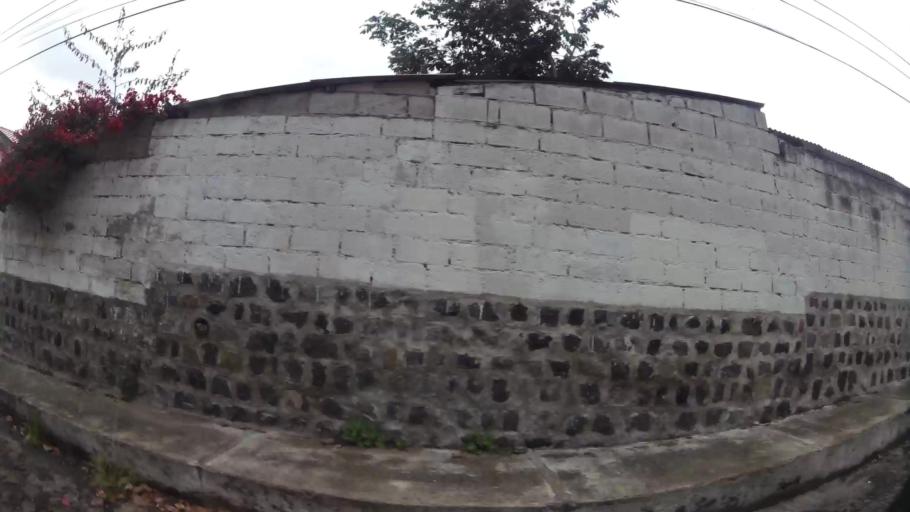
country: EC
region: Pichincha
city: Sangolqui
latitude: -0.2961
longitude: -78.4686
